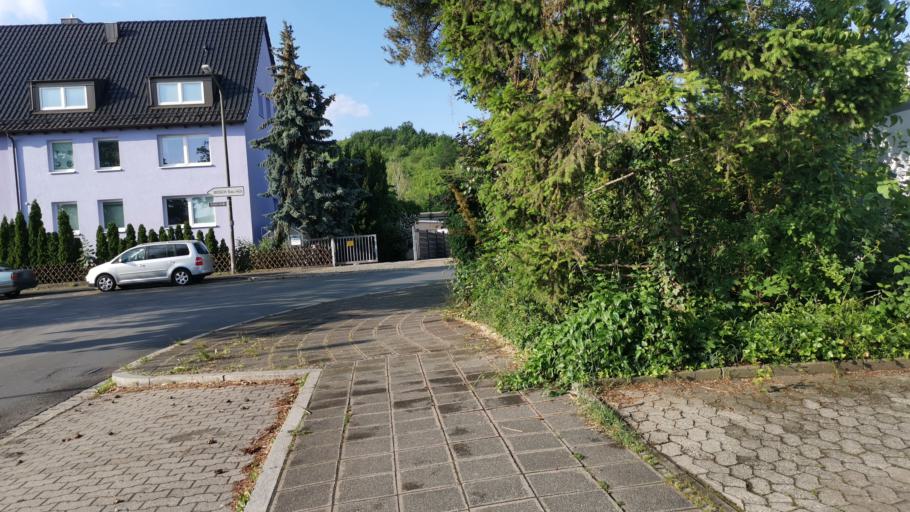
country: DE
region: Bavaria
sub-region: Regierungsbezirk Mittelfranken
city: Grossreuth bei Schweinau
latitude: 49.4241
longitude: 11.0463
